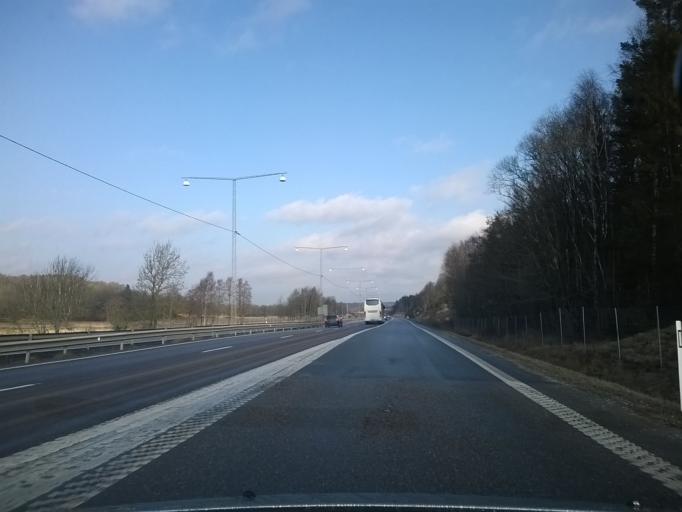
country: SE
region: Vaestra Goetaland
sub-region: Kungalvs Kommun
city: Kungalv
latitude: 57.8868
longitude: 11.9427
